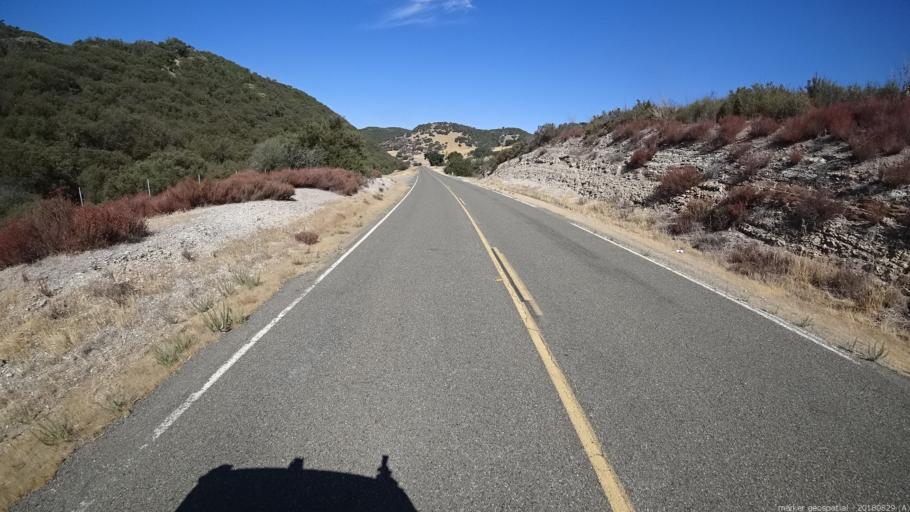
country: US
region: California
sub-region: San Luis Obispo County
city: Lake Nacimiento
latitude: 35.8556
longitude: -121.0577
